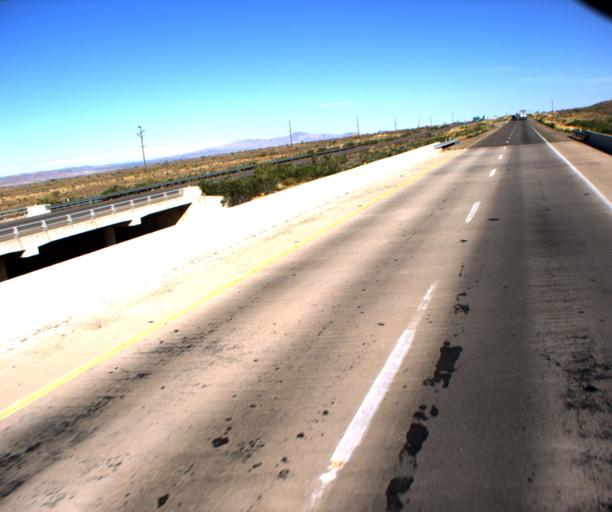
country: US
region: Arizona
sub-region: Mohave County
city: Dolan Springs
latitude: 35.4125
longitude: -114.2704
